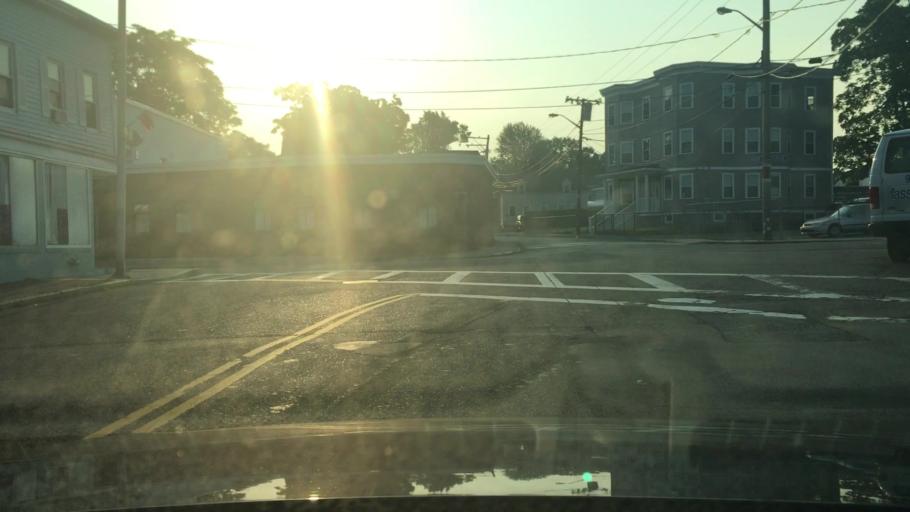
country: US
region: Massachusetts
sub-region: Essex County
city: Lynn
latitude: 42.4656
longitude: -70.9682
